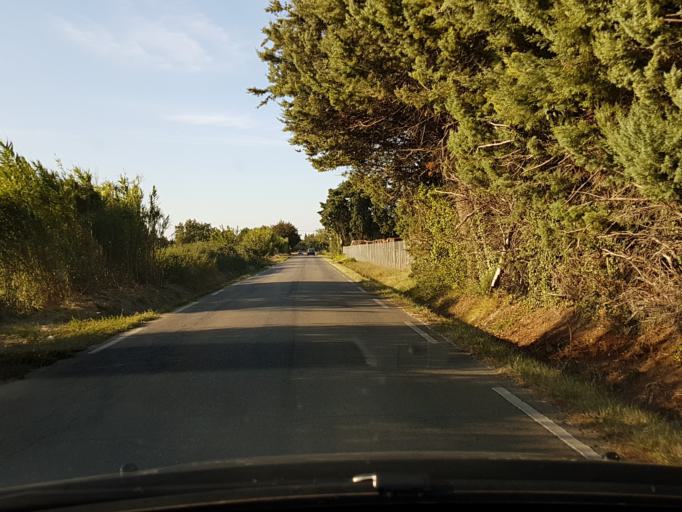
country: FR
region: Provence-Alpes-Cote d'Azur
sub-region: Departement des Bouches-du-Rhone
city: Molleges
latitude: 43.7968
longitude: 4.9535
